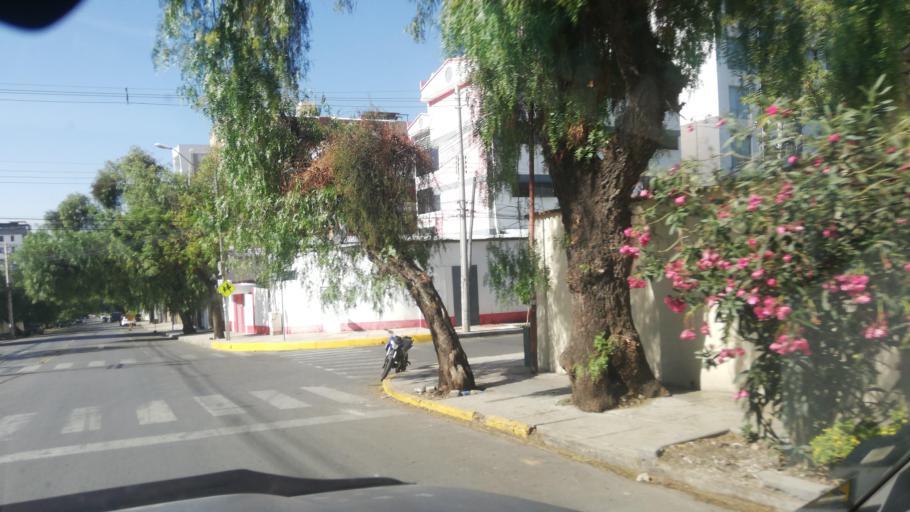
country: BO
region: Cochabamba
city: Cochabamba
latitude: -17.3673
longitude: -66.1565
